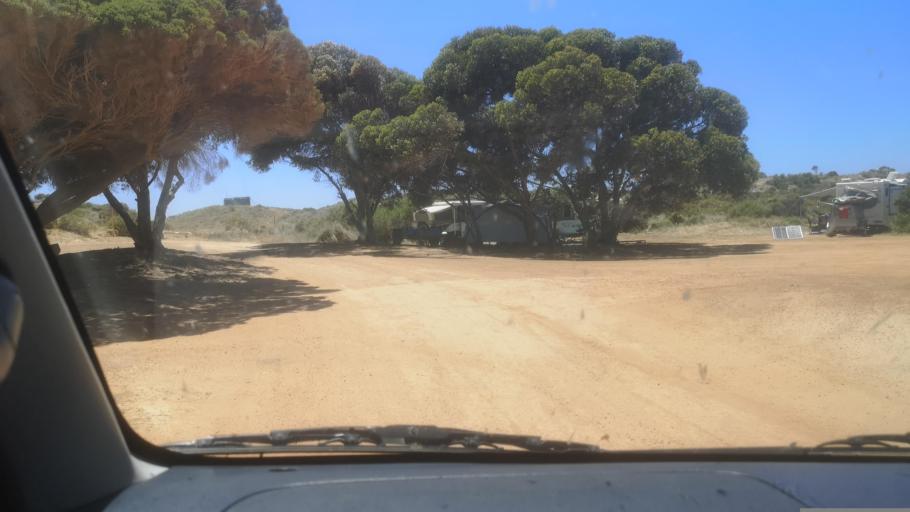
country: AU
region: Western Australia
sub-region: Dandaragan
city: Jurien Bay
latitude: -30.1841
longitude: 114.9981
